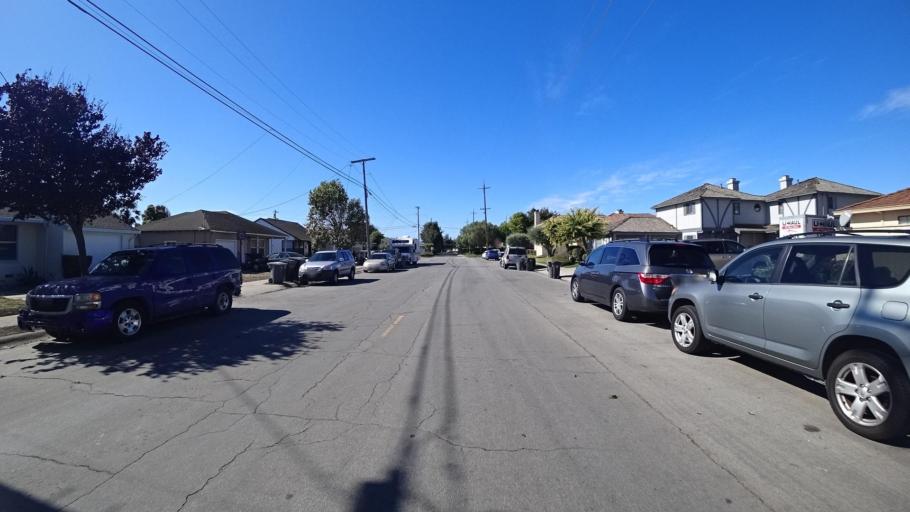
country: US
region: California
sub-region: Monterey County
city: Salinas
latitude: 36.6809
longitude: -121.6730
